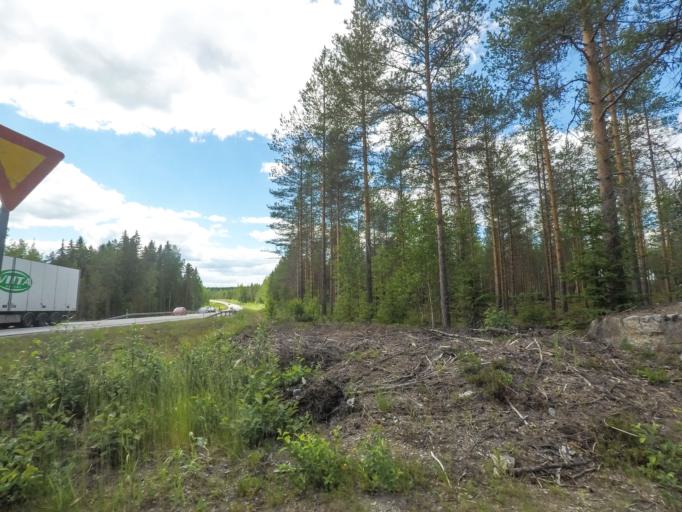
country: FI
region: Central Finland
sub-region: Jyvaeskylae
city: Hankasalmi
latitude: 62.4042
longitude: 26.6591
